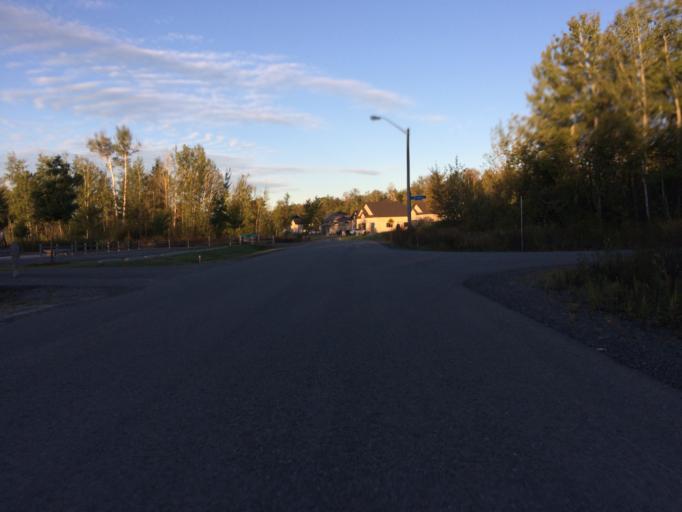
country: CA
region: Ontario
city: Ottawa
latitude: 45.2644
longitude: -75.5836
